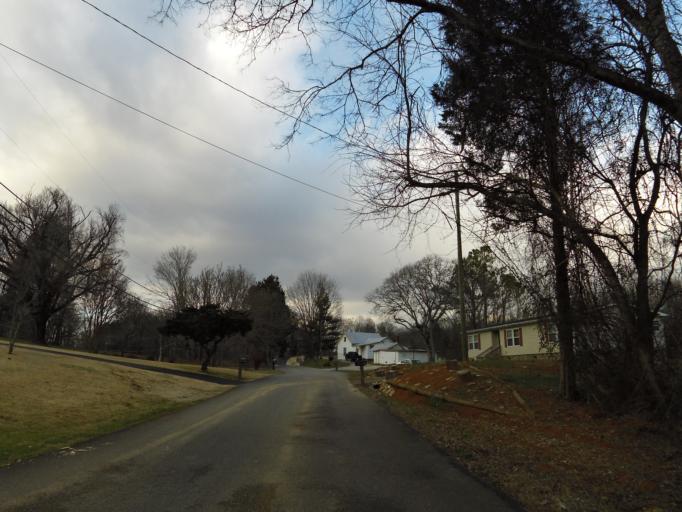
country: US
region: Tennessee
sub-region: Knox County
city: Knoxville
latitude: 35.9223
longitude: -83.8553
